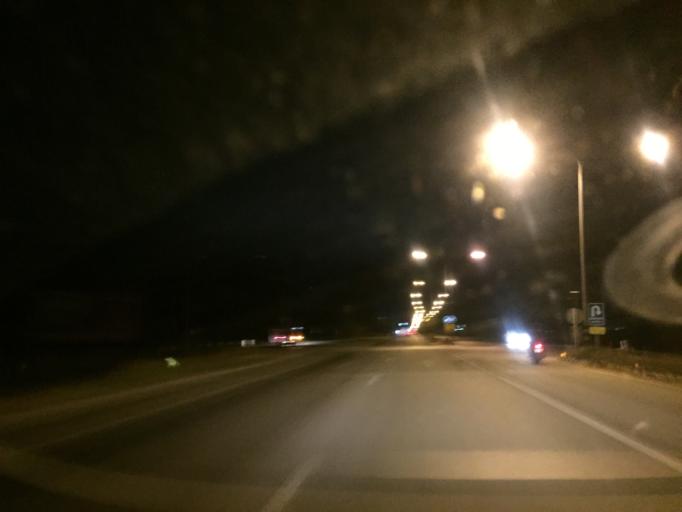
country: TH
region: Changwat Udon Thani
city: Udon Thani
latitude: 17.3655
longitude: 102.7074
